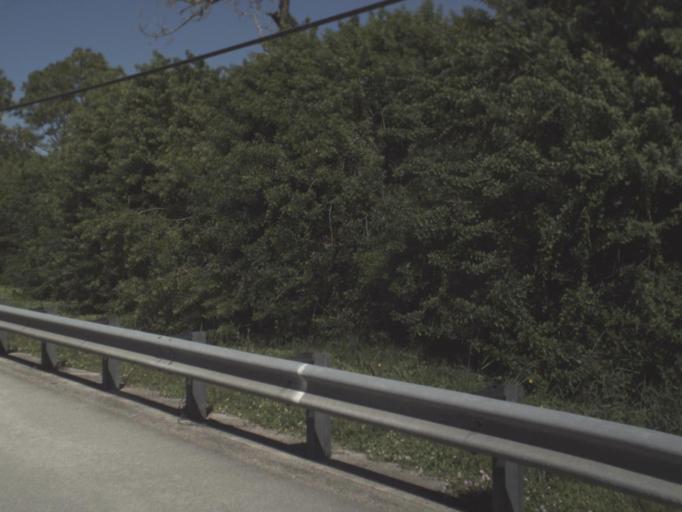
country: US
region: Florida
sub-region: Collier County
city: Lely Resort
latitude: 26.0172
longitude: -81.6270
